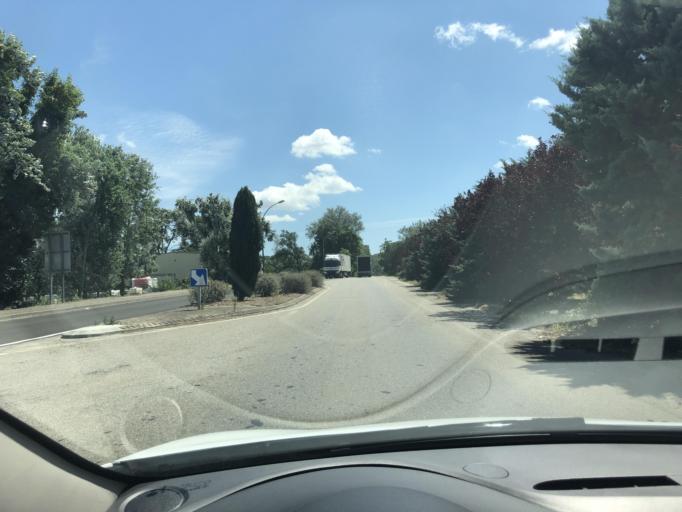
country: FR
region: Provence-Alpes-Cote d'Azur
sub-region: Departement des Bouches-du-Rhone
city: Noves
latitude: 43.8914
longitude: 4.8802
